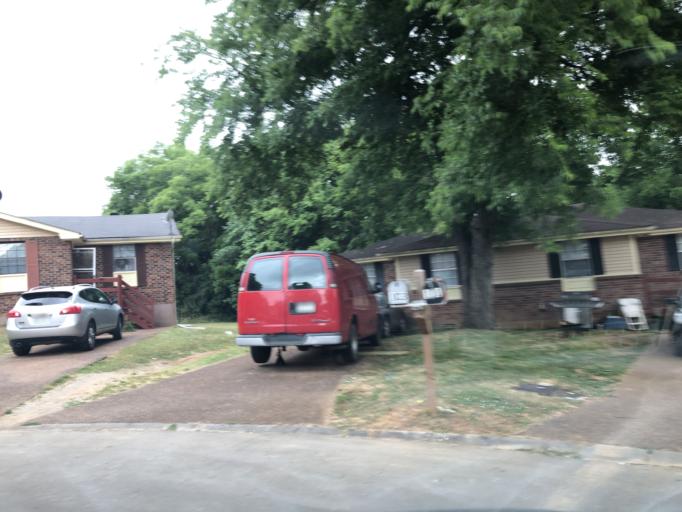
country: US
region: Tennessee
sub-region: Davidson County
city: Goodlettsville
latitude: 36.2855
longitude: -86.7179
